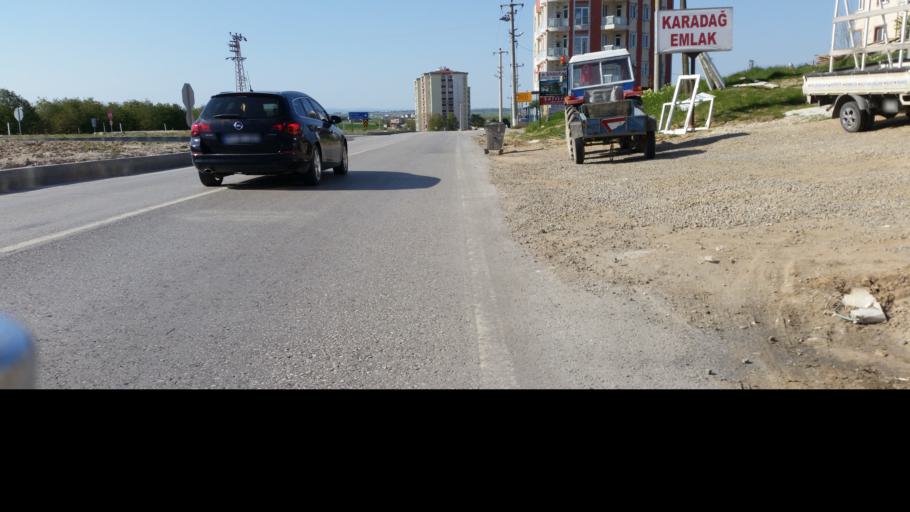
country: TR
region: Tekirdag
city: Saray
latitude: 41.3632
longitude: 27.9423
